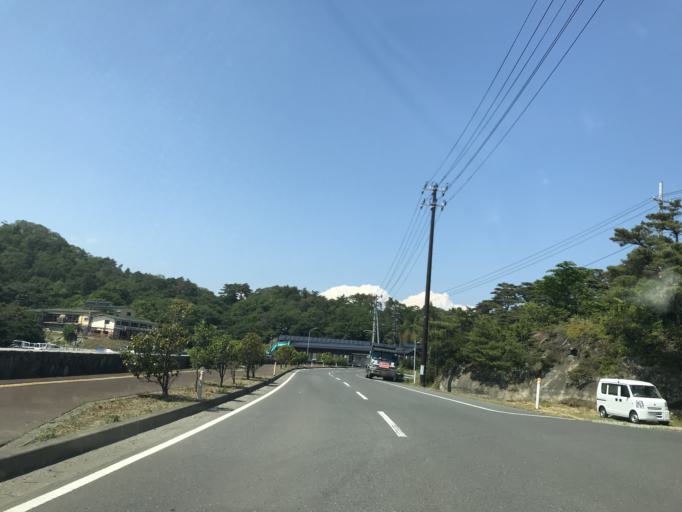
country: JP
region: Miyagi
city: Matsushima
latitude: 38.3415
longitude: 141.1493
